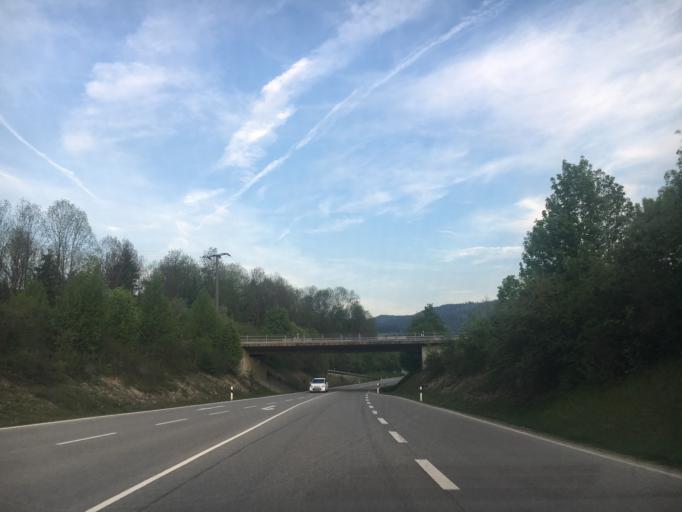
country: DE
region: Bavaria
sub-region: Upper Bavaria
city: Bichl
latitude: 47.7286
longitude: 11.4162
